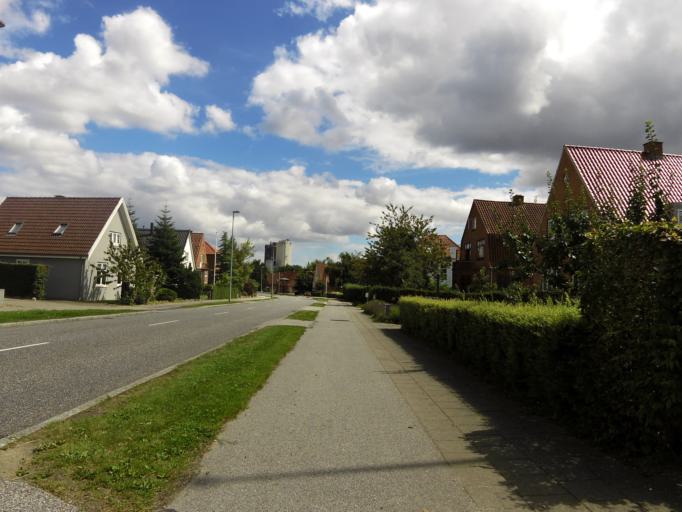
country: DK
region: South Denmark
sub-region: Haderslev Kommune
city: Haderslev
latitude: 55.2515
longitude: 9.4652
